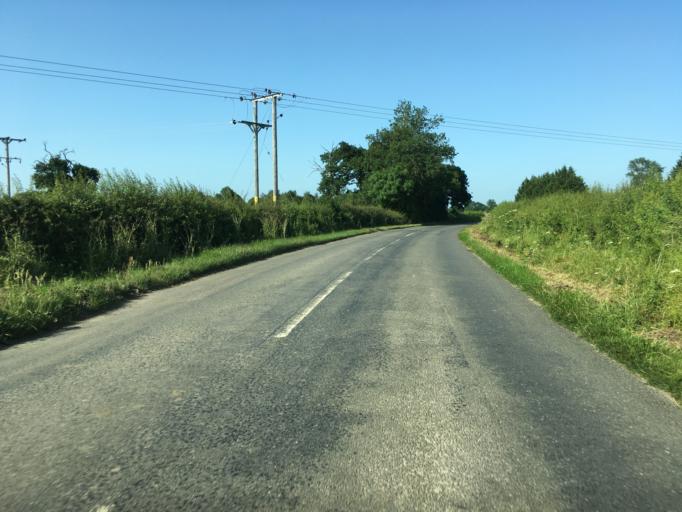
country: GB
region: England
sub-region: Buckinghamshire
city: Steeple Claydon
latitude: 51.9323
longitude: -1.0199
